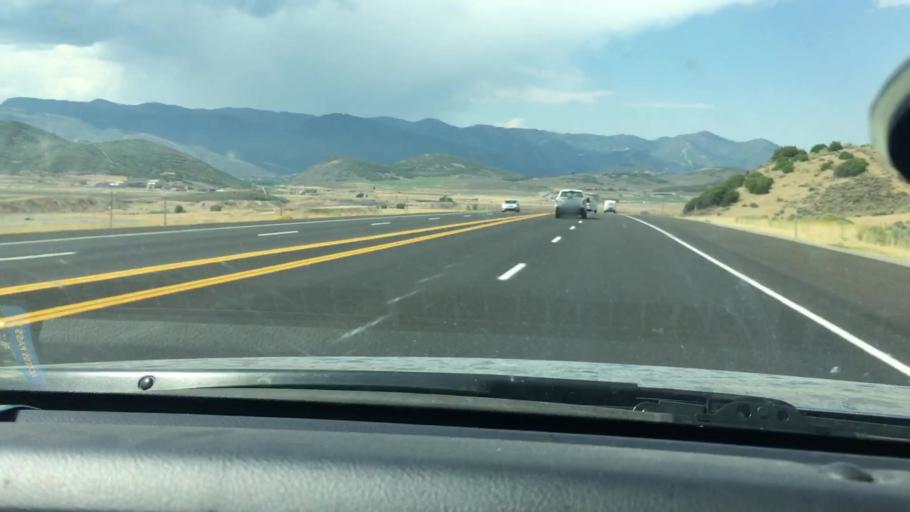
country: US
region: Utah
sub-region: Summit County
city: Park City
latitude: 40.6810
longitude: -111.4388
